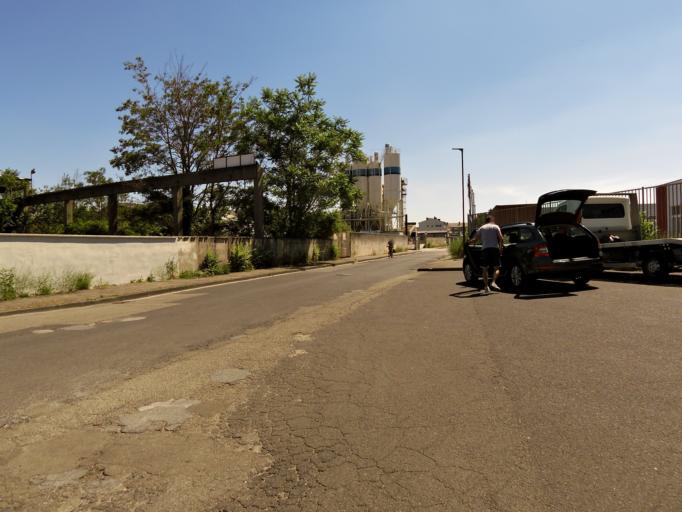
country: DE
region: Rheinland-Pfalz
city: Neustadt
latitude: 49.3541
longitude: 8.1630
